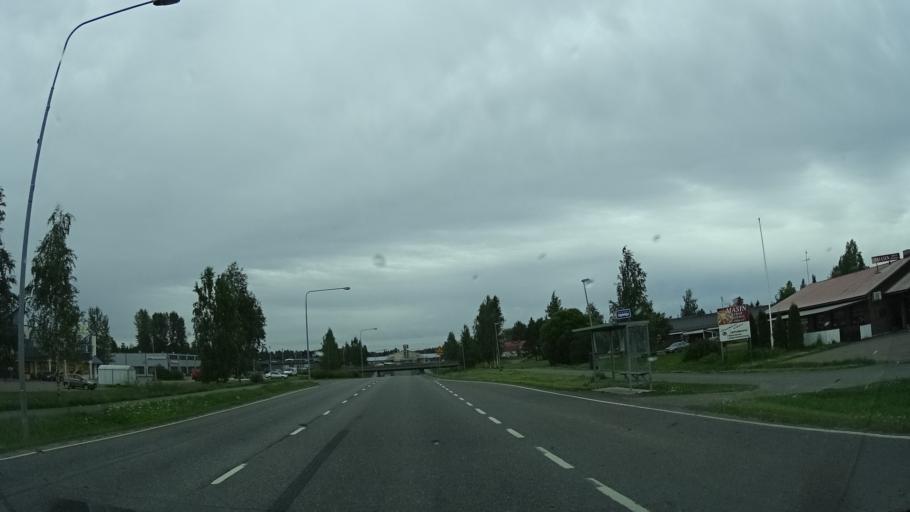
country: FI
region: Varsinais-Suomi
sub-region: Loimaa
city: Aura
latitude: 60.6493
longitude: 22.5871
